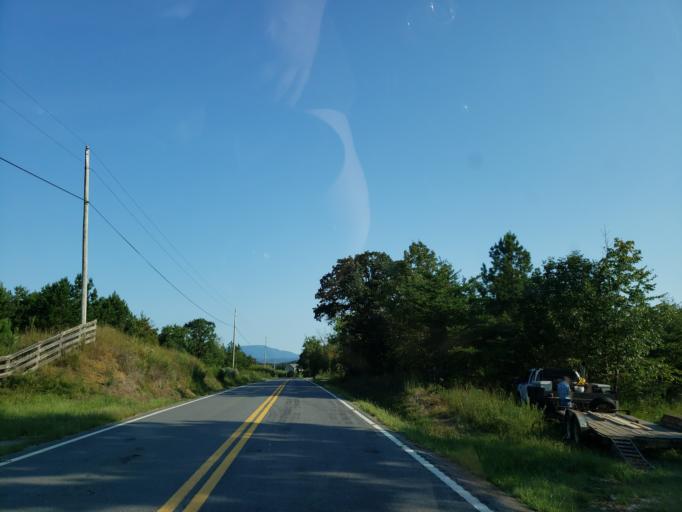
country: US
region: Tennessee
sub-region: Bradley County
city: Wildwood Lake
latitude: 35.0207
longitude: -84.7939
